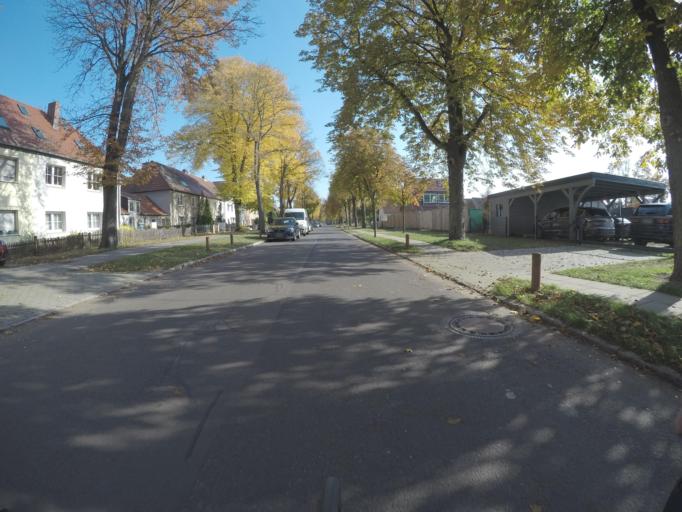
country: DE
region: Brandenburg
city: Hohen Neuendorf
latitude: 52.6807
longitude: 13.2478
